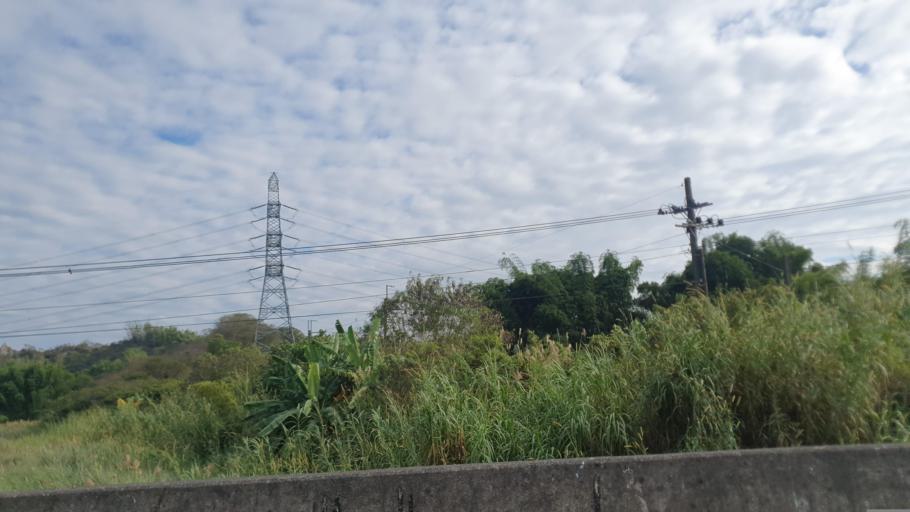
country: TW
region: Taiwan
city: Yujing
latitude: 23.0354
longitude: 120.4166
